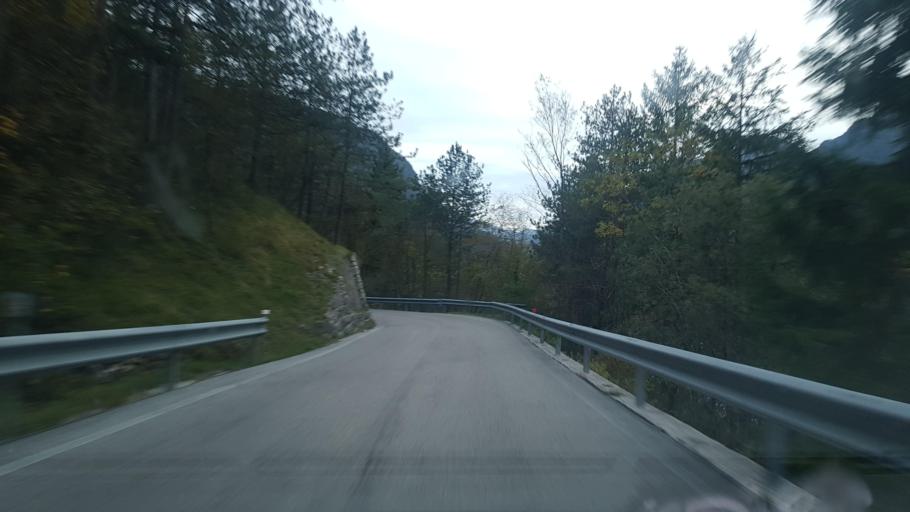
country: IT
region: Friuli Venezia Giulia
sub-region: Provincia di Udine
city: Chiaulis
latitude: 46.3231
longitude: 12.9407
